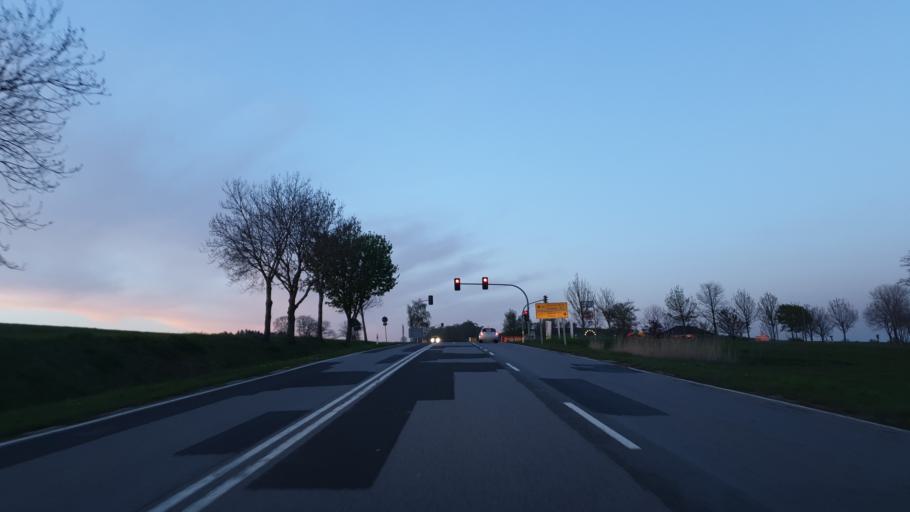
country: DE
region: Saxony
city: Lossnitz
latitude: 50.6457
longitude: 12.7439
